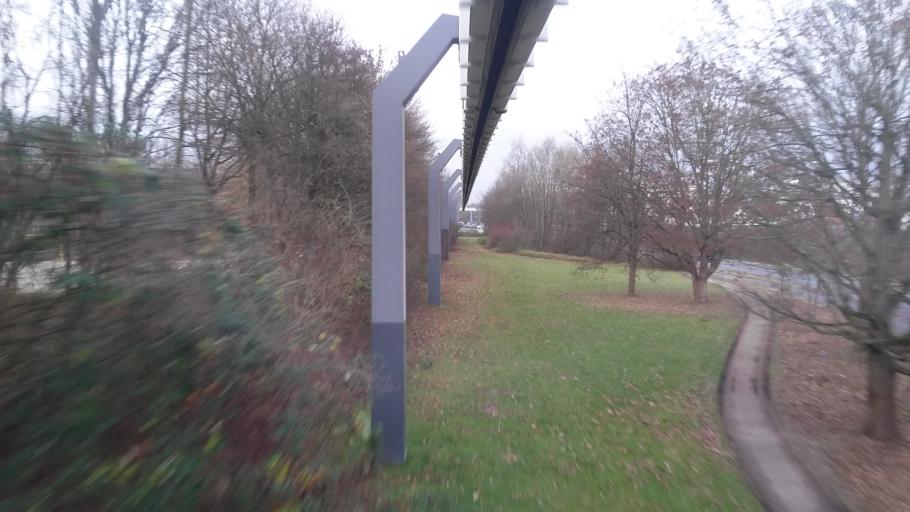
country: DE
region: North Rhine-Westphalia
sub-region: Regierungsbezirk Arnsberg
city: Dortmund
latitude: 51.4884
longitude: 7.4174
